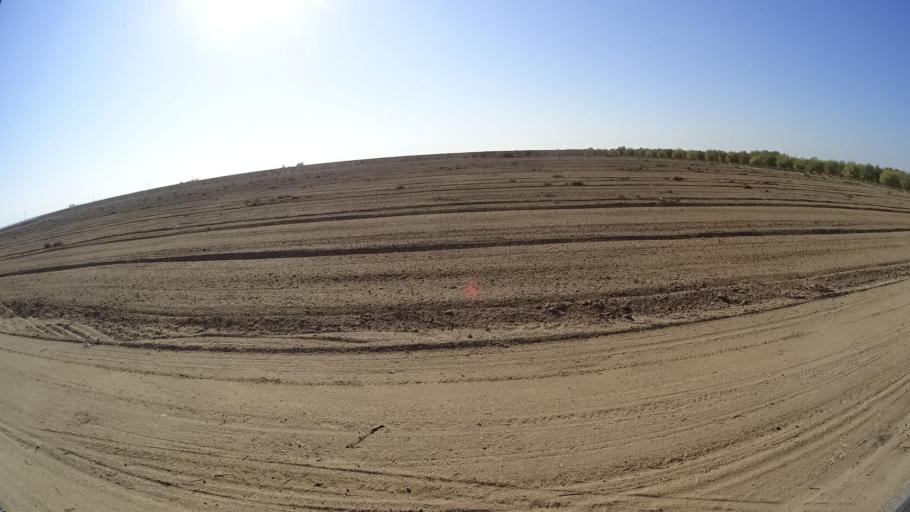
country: US
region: California
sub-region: Kern County
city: Delano
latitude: 35.7399
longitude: -119.2179
